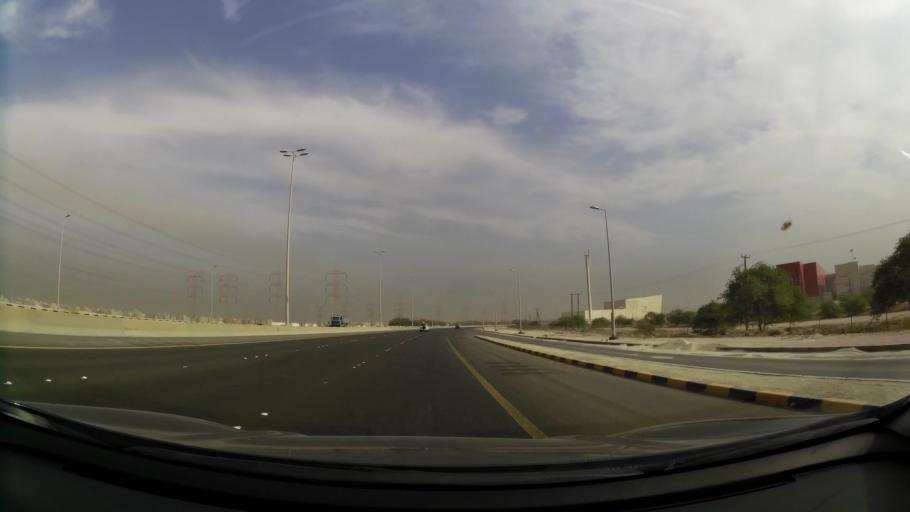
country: KW
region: Muhafazat al Jahra'
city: Al Jahra'
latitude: 29.3229
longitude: 47.7855
